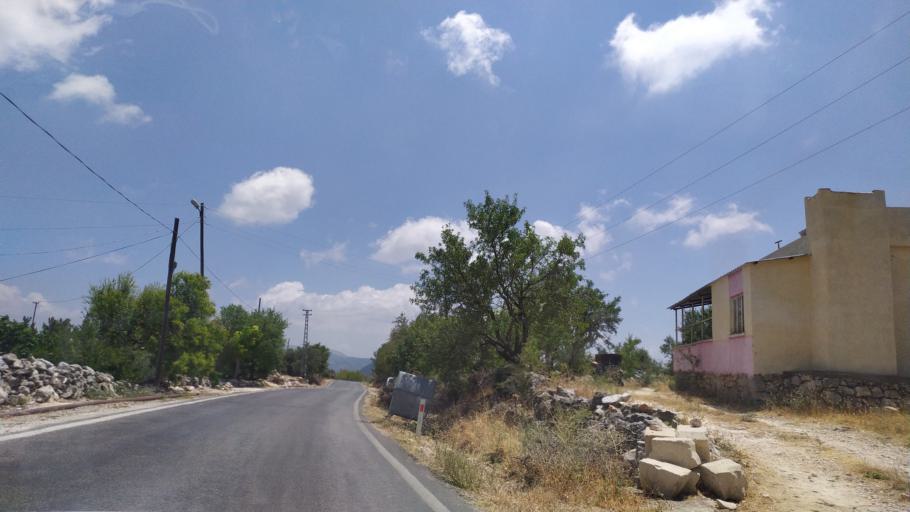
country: TR
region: Mersin
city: Gulnar
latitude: 36.2840
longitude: 33.3863
